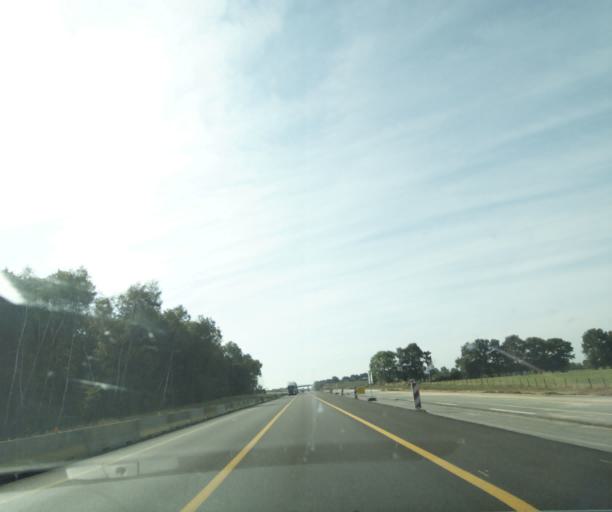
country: FR
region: Bourgogne
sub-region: Departement de Saone-et-Loire
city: Palinges
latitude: 46.5192
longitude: 4.1638
